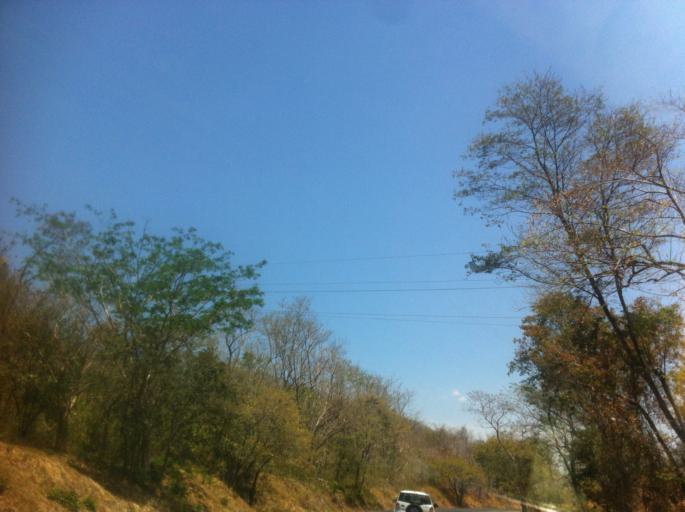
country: CR
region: Guanacaste
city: Belen
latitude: 10.3701
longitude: -85.5774
